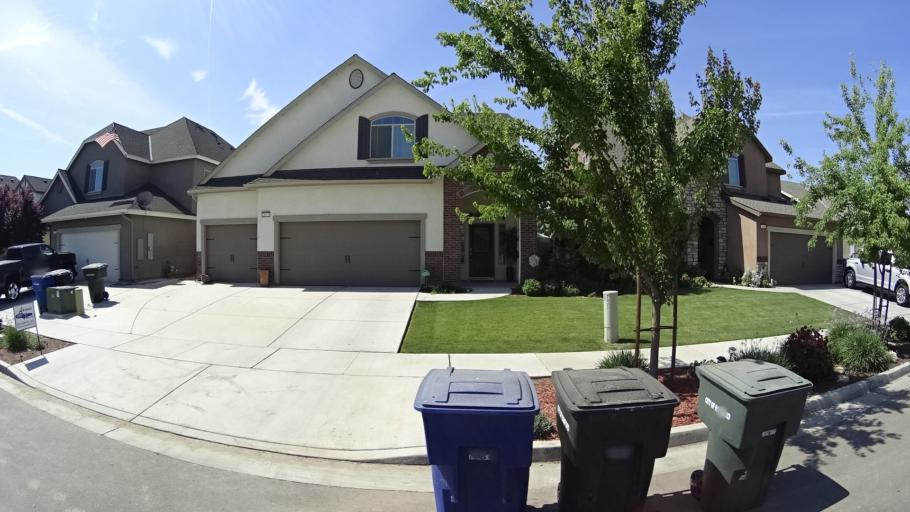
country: US
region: California
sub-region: Kings County
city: Hanford
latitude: 36.3357
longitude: -119.6794
